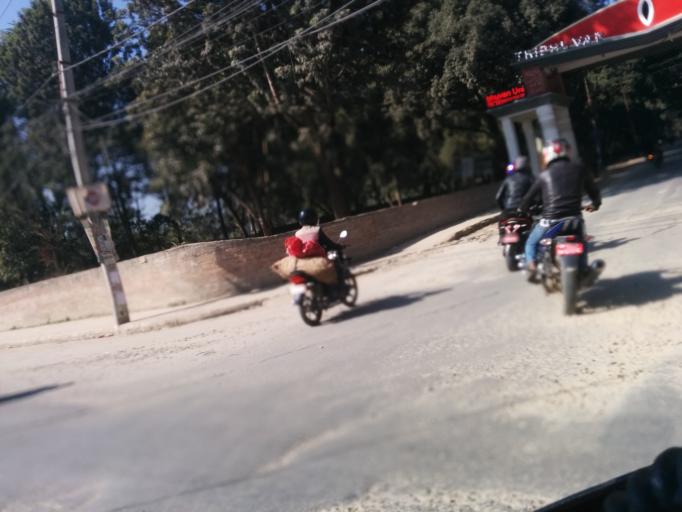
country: NP
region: Central Region
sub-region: Bagmati Zone
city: Patan
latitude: 27.6787
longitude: 85.2971
